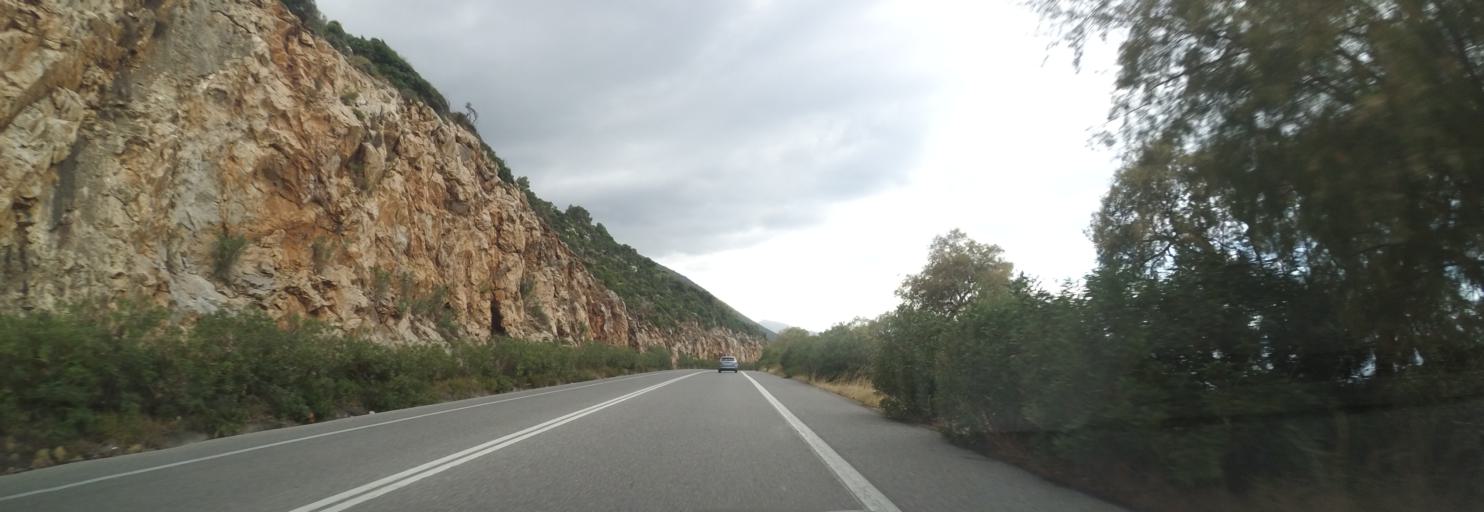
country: GR
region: Crete
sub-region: Nomos Rethymnis
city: Zoniana
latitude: 35.4050
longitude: 24.8536
